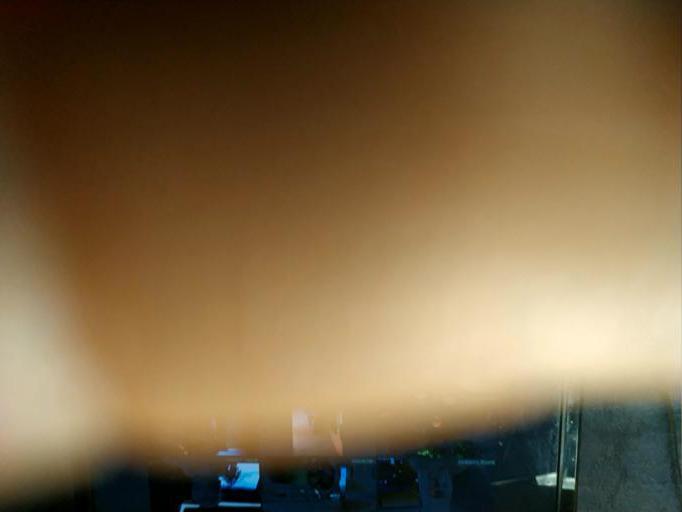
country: RU
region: Tverskaya
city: Ves'yegonsk
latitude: 58.7002
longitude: 37.5439
